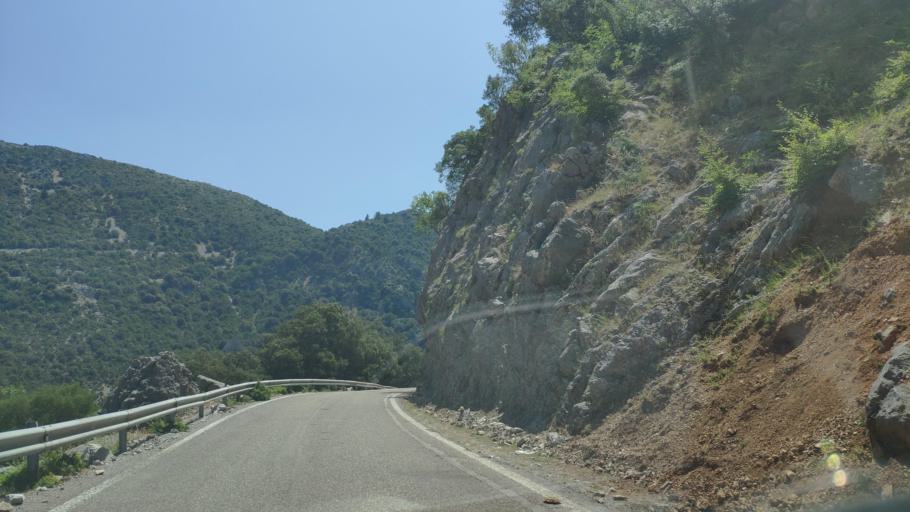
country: GR
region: West Greece
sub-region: Nomos Aitolias kai Akarnanias
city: Krikellos
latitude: 39.0178
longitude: 21.3513
